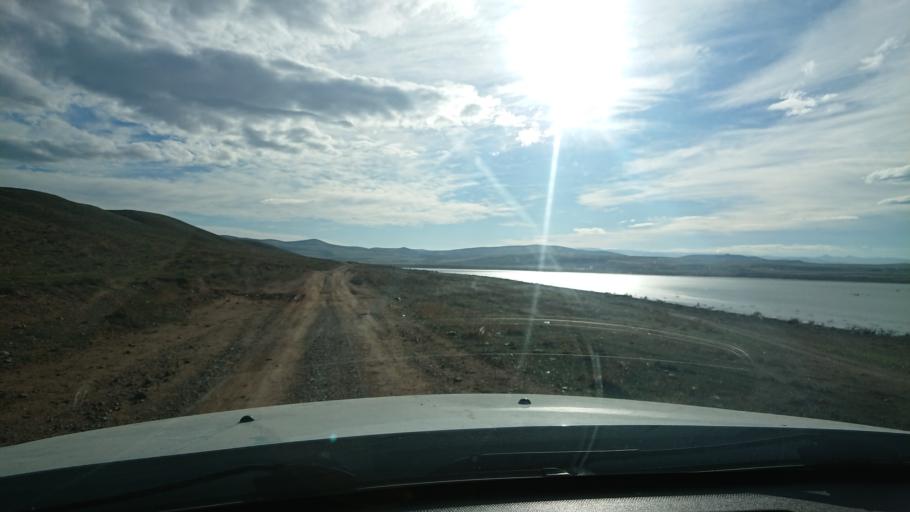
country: TR
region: Aksaray
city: Sariyahsi
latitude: 39.0485
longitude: 33.9737
